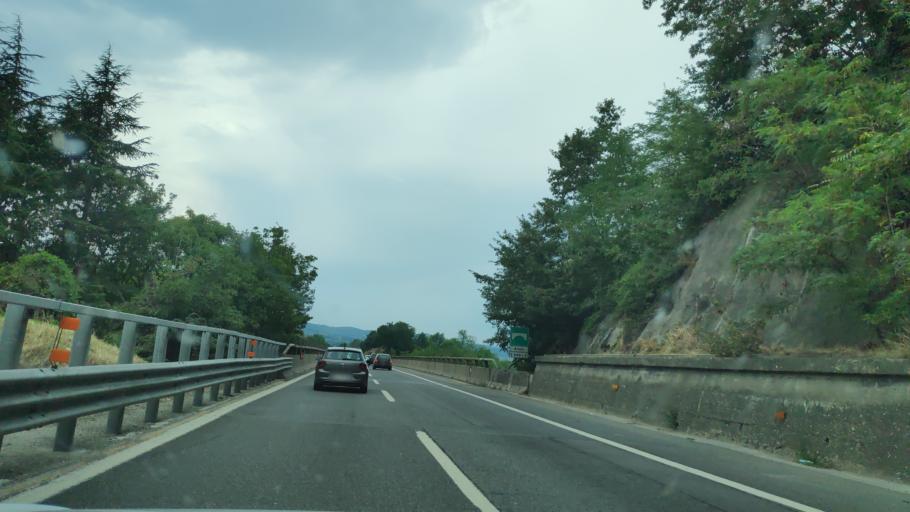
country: IT
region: Tuscany
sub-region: Province of Florence
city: Incisa in Val d'Arno
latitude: 43.6748
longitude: 11.4541
